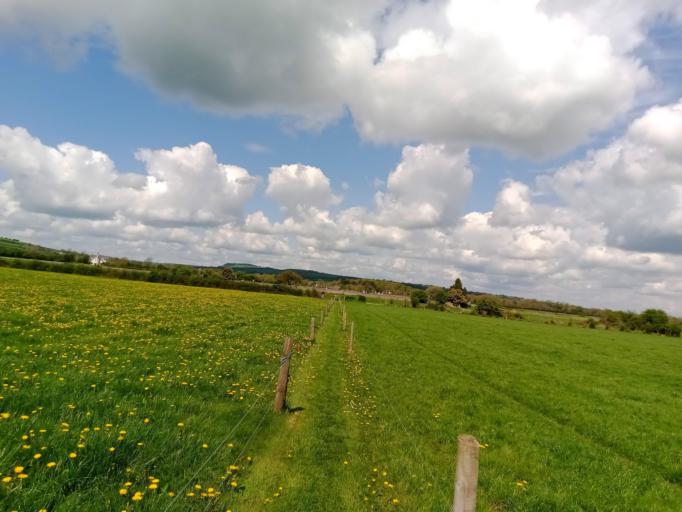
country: IE
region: Leinster
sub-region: Kilkenny
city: Ballyragget
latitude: 52.7337
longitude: -7.4165
